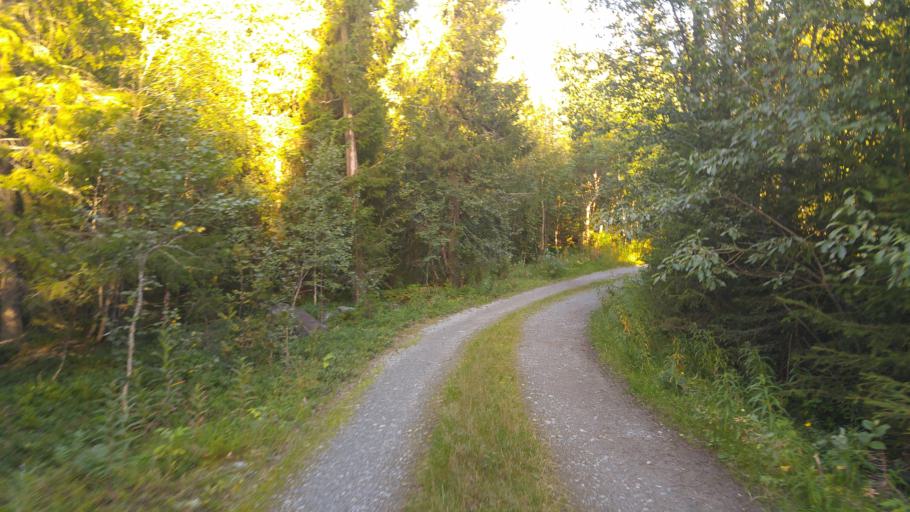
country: NO
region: Buskerud
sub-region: Hemsedal
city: Troim
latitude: 60.8514
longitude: 8.6118
